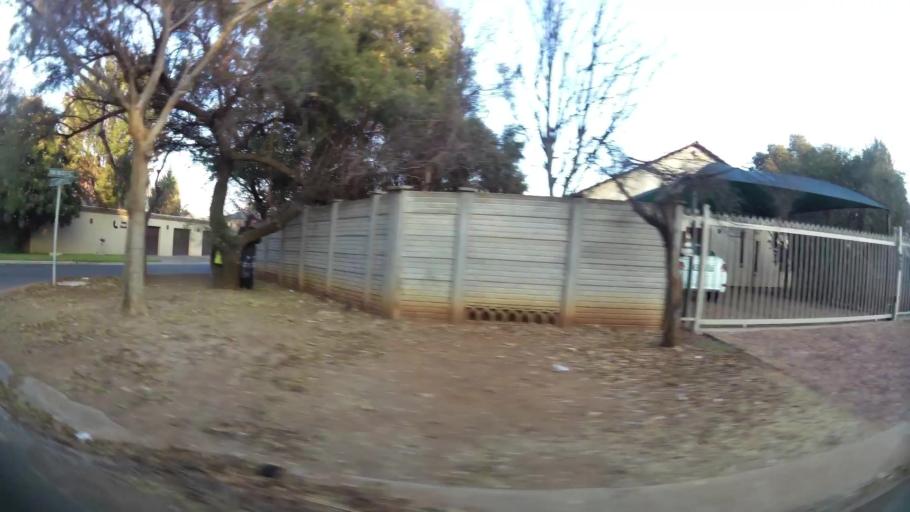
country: ZA
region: Orange Free State
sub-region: Mangaung Metropolitan Municipality
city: Bloemfontein
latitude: -29.1056
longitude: 26.1546
